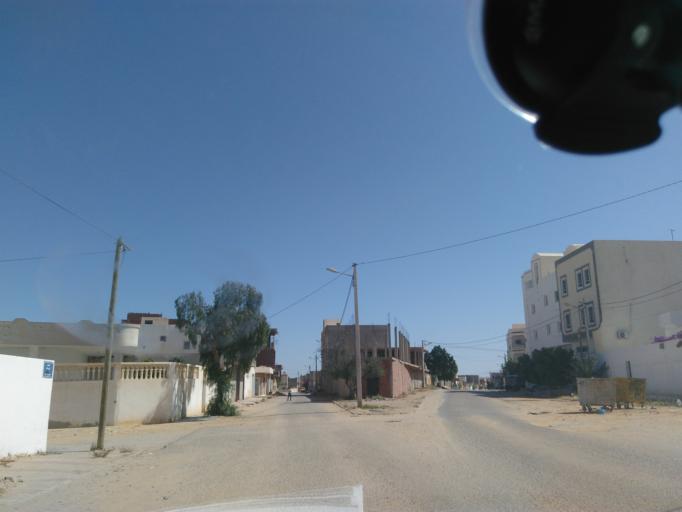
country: TN
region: Tataouine
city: Tataouine
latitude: 32.9464
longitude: 10.4651
